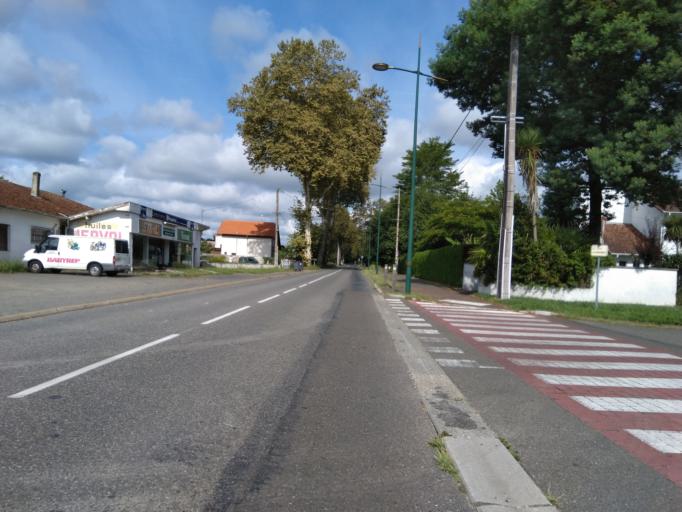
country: FR
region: Aquitaine
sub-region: Departement des Landes
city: Mees
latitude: 43.7282
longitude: -1.0870
